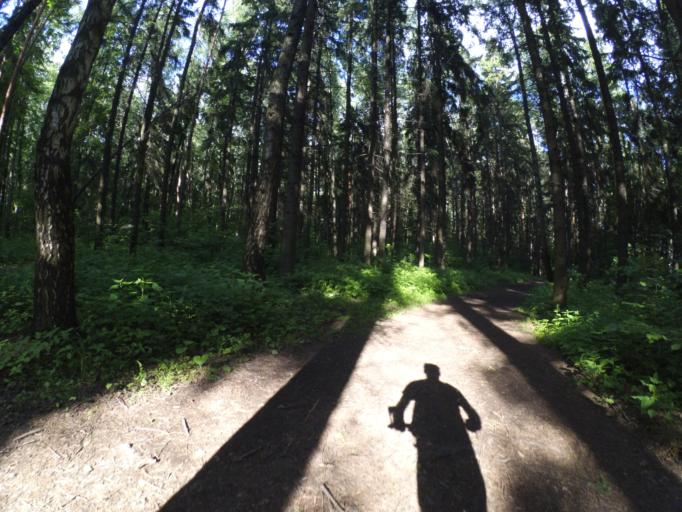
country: RU
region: Moscow
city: Davydkovo
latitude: 55.7281
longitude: 37.4868
